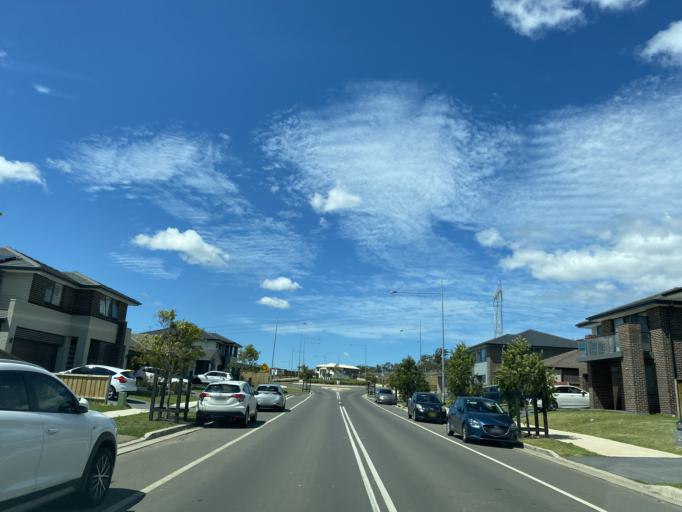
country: AU
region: New South Wales
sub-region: Camden
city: Narellan Vale
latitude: -34.0141
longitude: 150.7843
